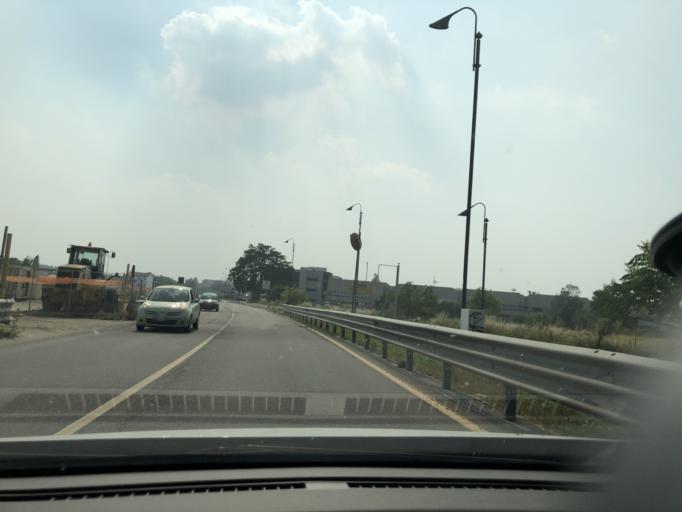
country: IT
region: Lombardy
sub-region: Citta metropolitana di Milano
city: Segrate
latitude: 45.4846
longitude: 9.2811
